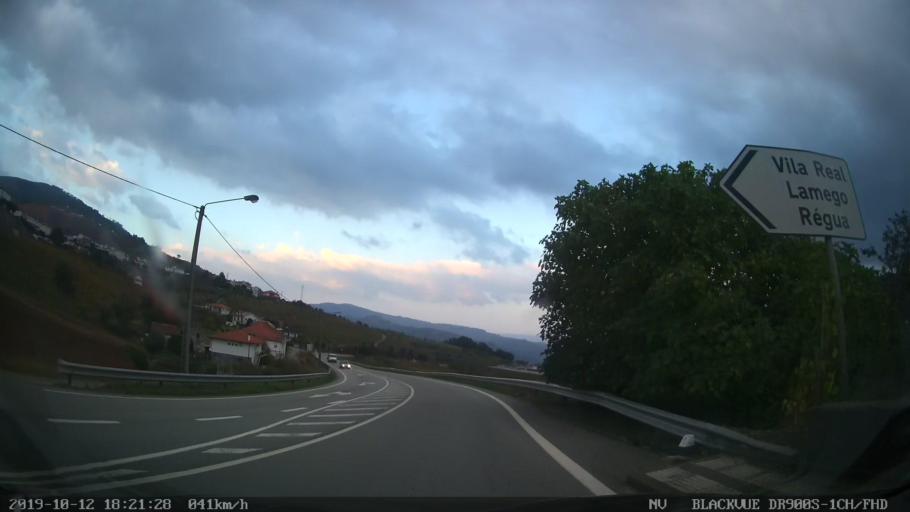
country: PT
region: Vila Real
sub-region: Mesao Frio
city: Mesao Frio
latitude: 41.1561
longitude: -7.8916
